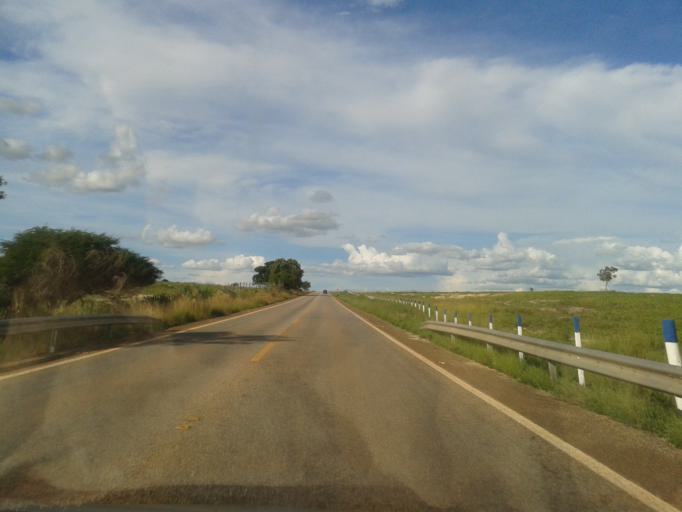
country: BR
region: Goias
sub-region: Mozarlandia
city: Mozarlandia
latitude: -14.3435
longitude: -50.4194
